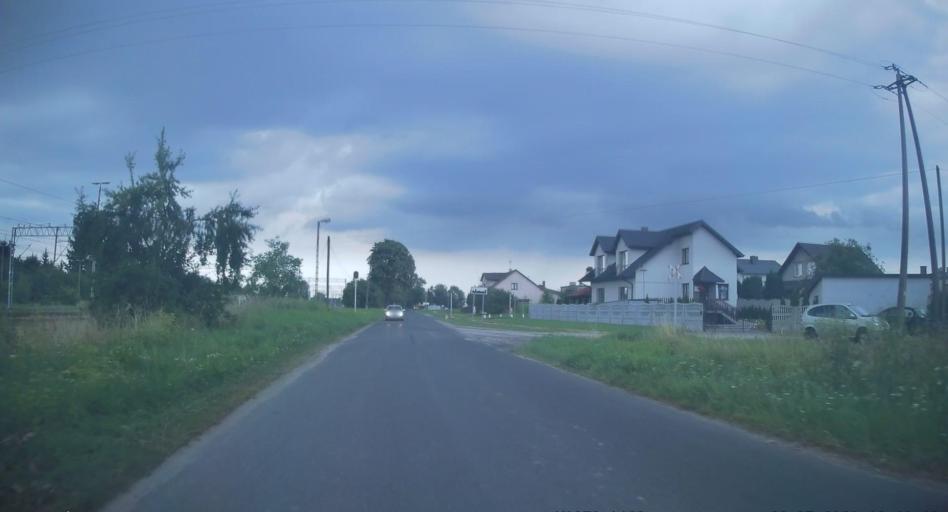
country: PL
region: Lodz Voivodeship
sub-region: Powiat brzezinski
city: Rogow
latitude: 51.8149
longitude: 19.8825
